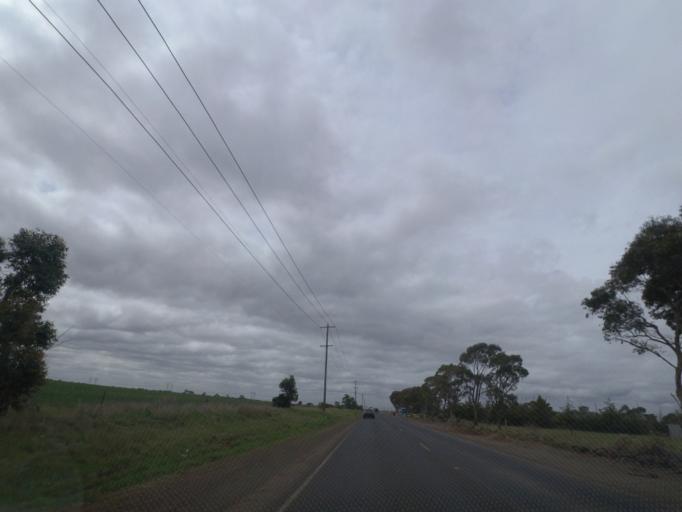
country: AU
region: Victoria
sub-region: Melton
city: Rockbank
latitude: -37.7178
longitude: 144.7023
